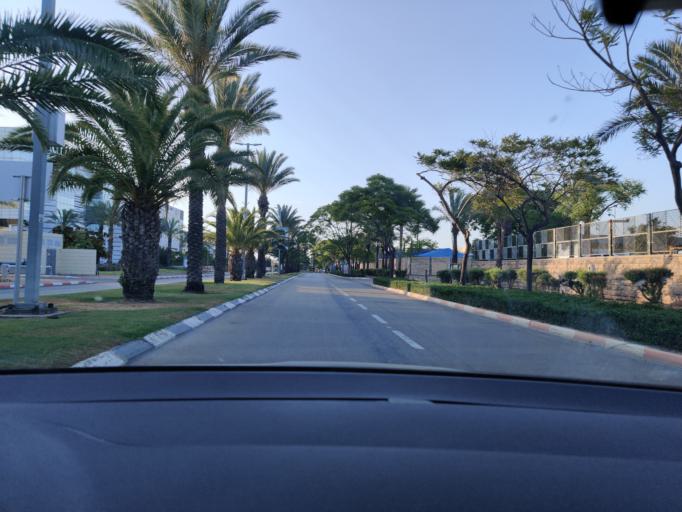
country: IL
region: Haifa
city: Qesarya
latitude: 32.4823
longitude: 34.9482
